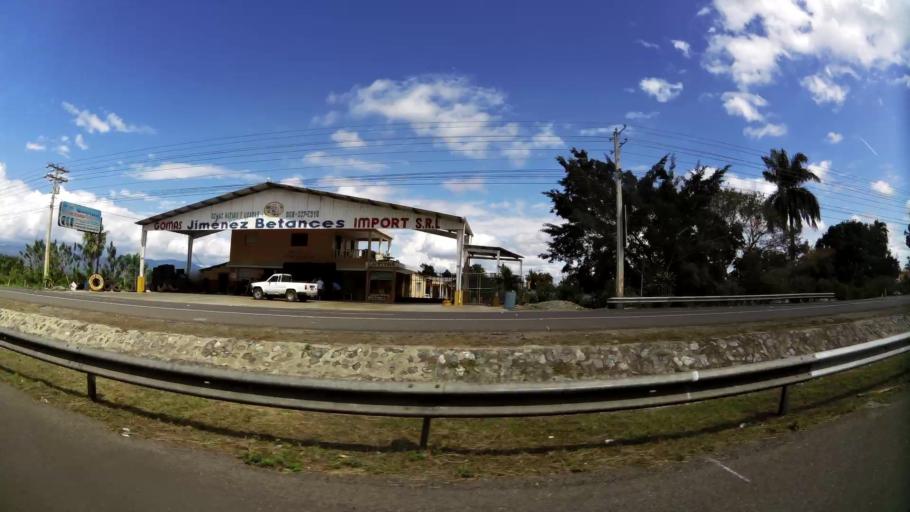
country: DO
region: Santiago
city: Licey al Medio
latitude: 19.3705
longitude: -70.6039
